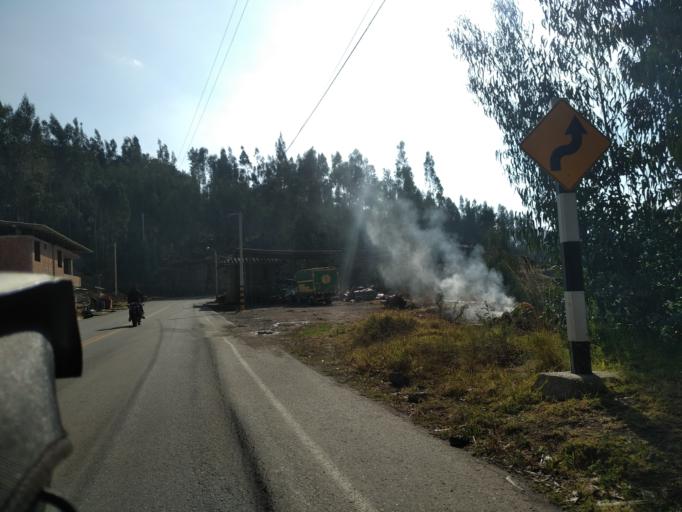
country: PE
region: La Libertad
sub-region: Provincia de Otuzco
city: Agallpampa
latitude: -7.9958
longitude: -78.5112
